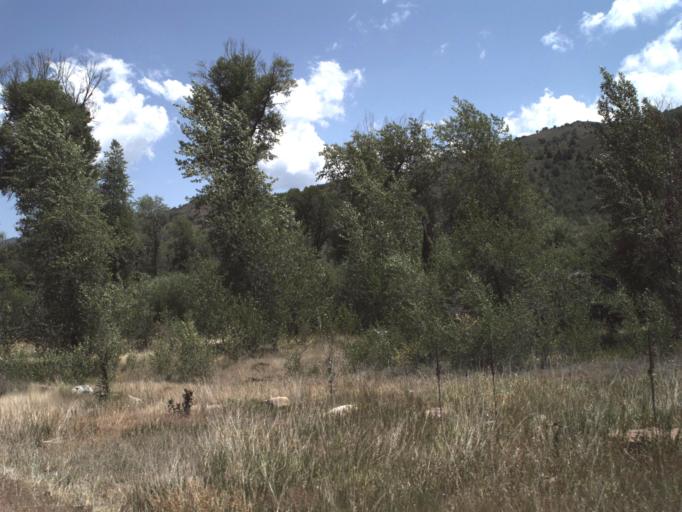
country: US
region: Utah
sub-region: Weber County
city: Wolf Creek
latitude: 41.2899
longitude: -111.6403
